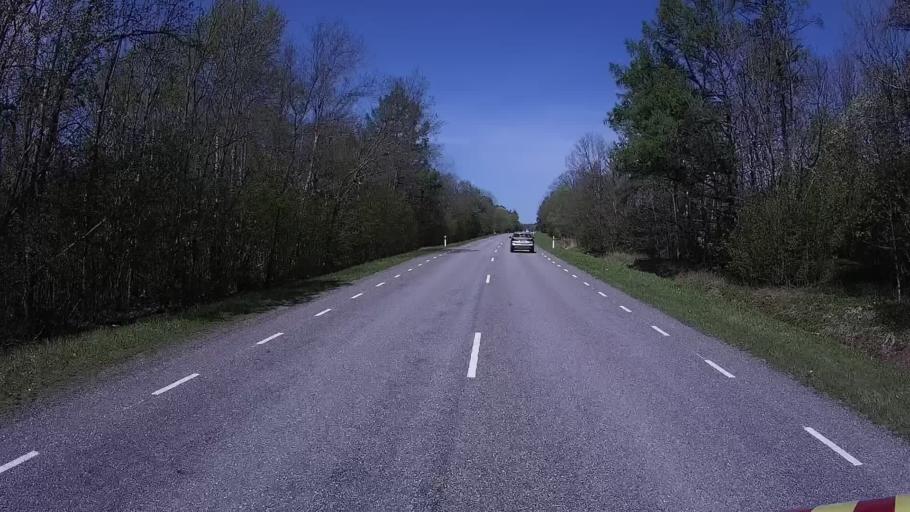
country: EE
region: Laeaene
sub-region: Lihula vald
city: Lihula
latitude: 58.7943
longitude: 23.8636
